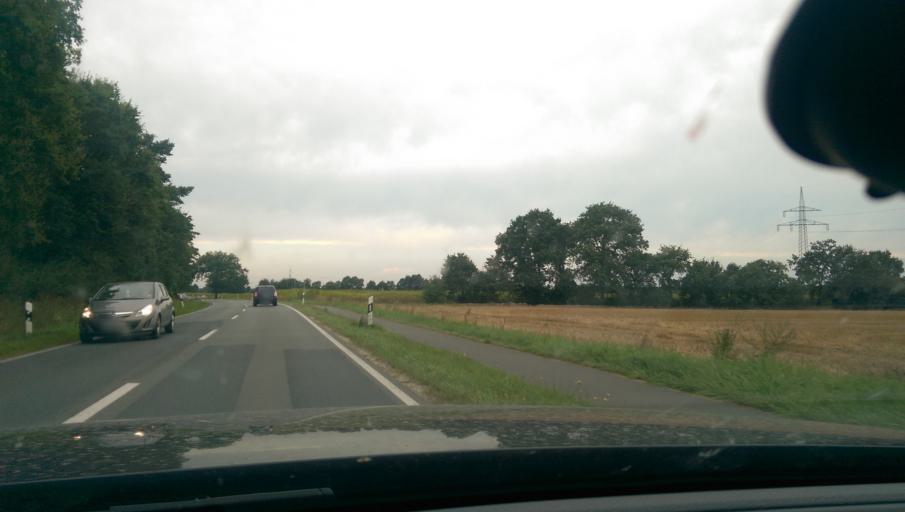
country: DE
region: Lower Saxony
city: Rehburg-Loccum
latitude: 52.4684
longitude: 9.1938
